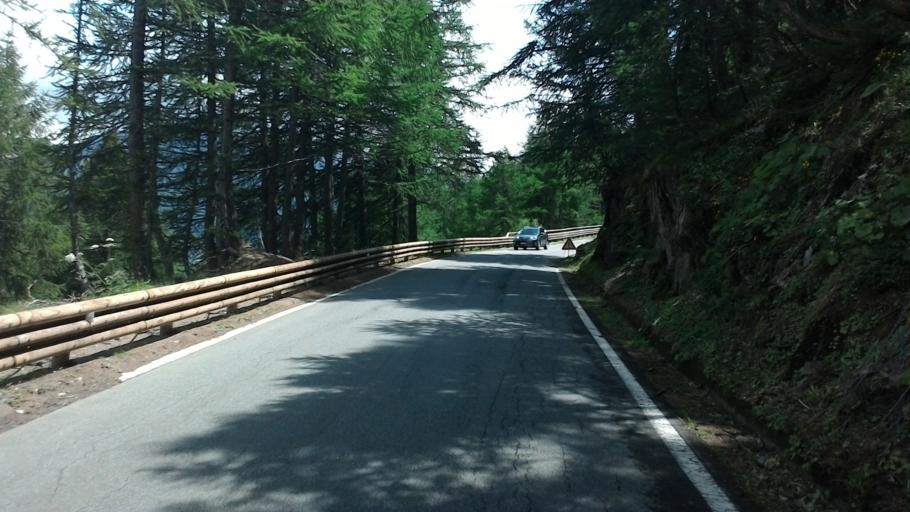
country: IT
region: Aosta Valley
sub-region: Valle d'Aosta
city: La Thuile
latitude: 45.7082
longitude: 6.9107
